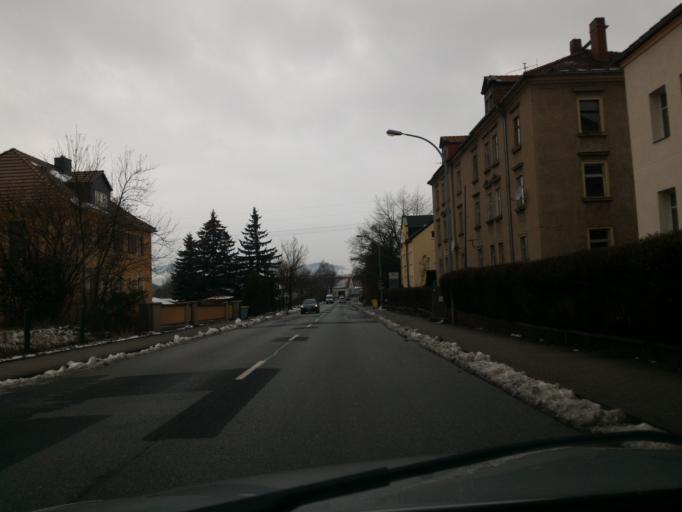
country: DE
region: Saxony
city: Olbersdorf
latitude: 50.8999
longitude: 14.7729
